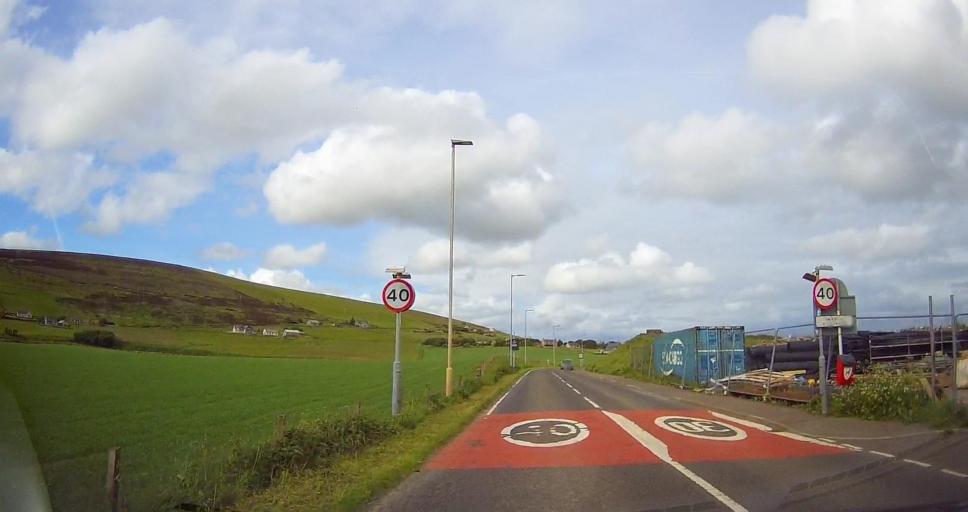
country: GB
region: Scotland
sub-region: Orkney Islands
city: Orkney
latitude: 59.0086
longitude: -3.1151
